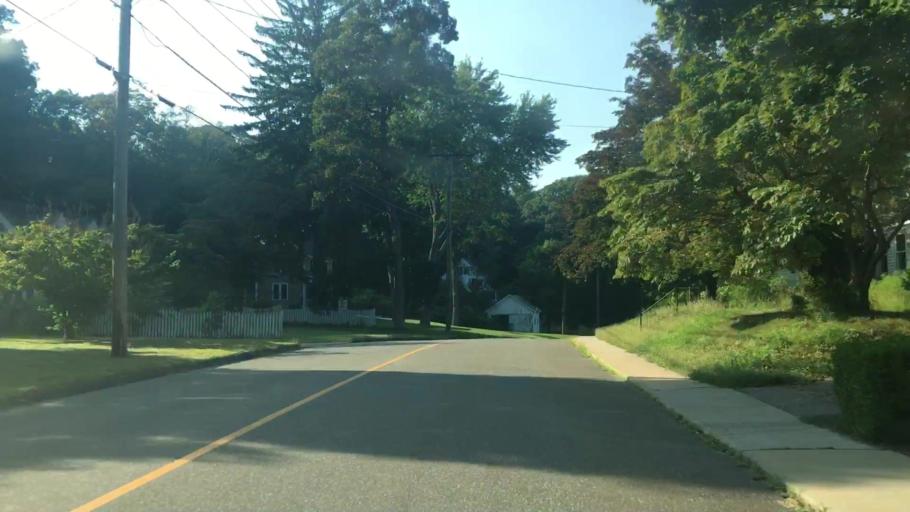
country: US
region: Connecticut
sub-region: Middlesex County
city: Deep River Center
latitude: 41.3875
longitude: -72.4437
